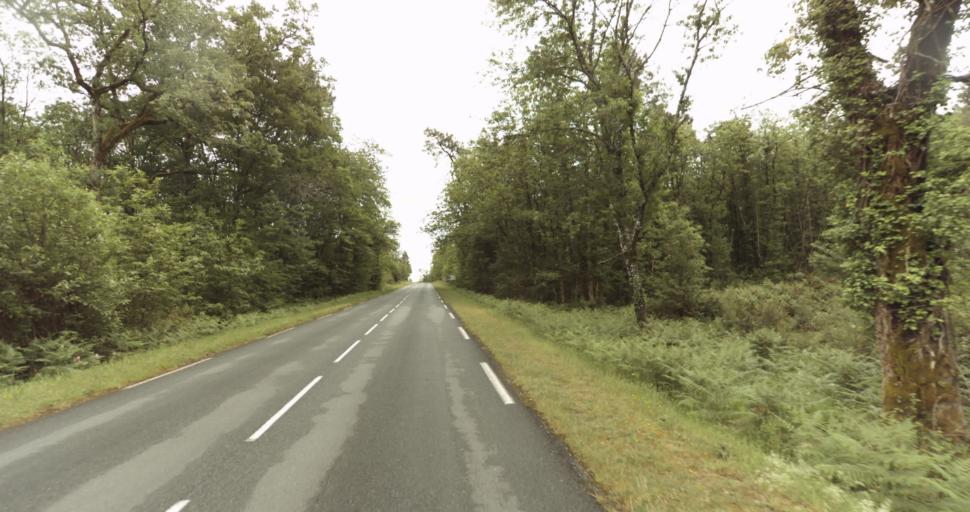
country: FR
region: Aquitaine
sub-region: Departement de la Dordogne
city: Belves
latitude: 44.6731
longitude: 0.9977
